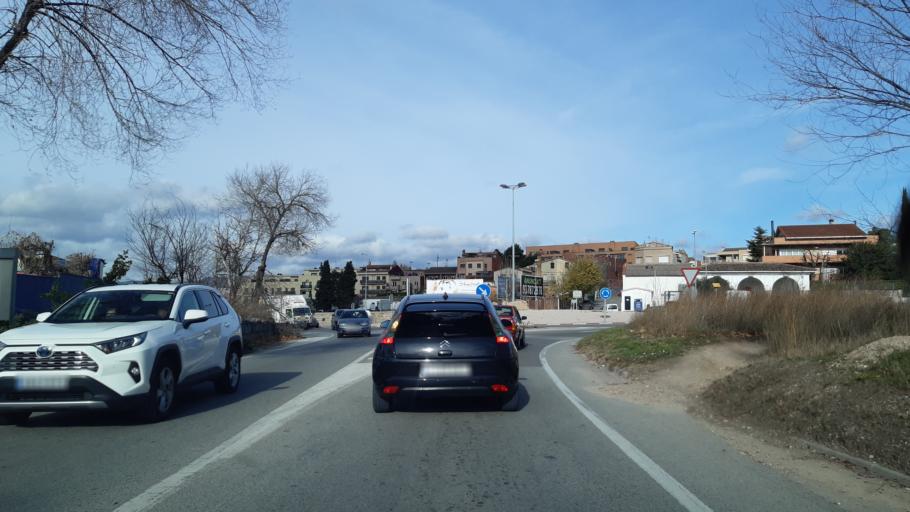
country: ES
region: Catalonia
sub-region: Provincia de Barcelona
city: Vilanova del Cami
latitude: 41.5777
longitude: 1.6400
